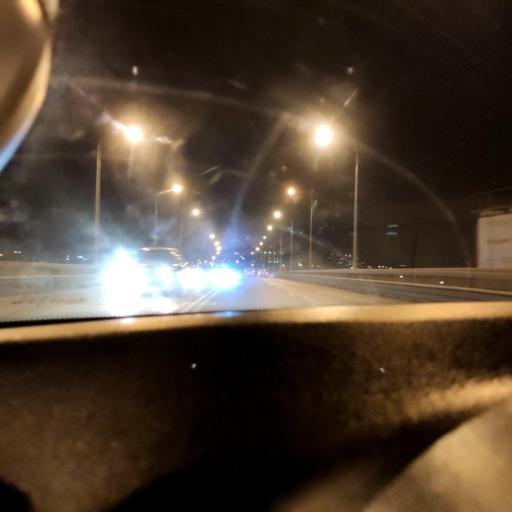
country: RU
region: Samara
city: Samara
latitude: 53.1748
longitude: 50.1937
